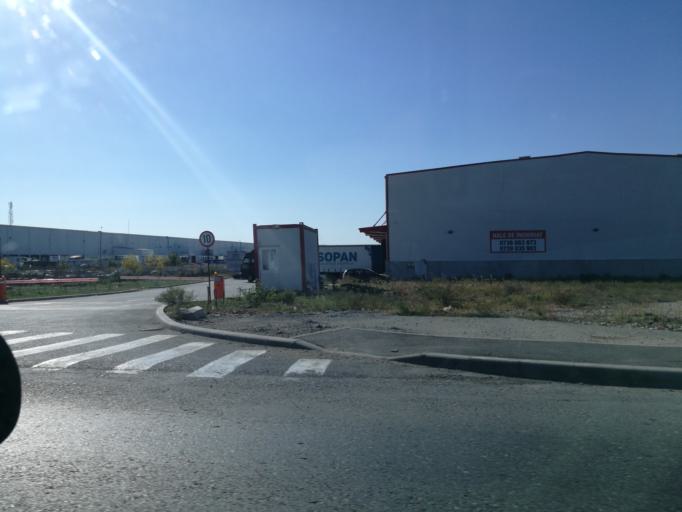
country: RO
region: Ilfov
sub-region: Comuna Chiajna
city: Chiajna
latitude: 44.4456
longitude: 25.9659
